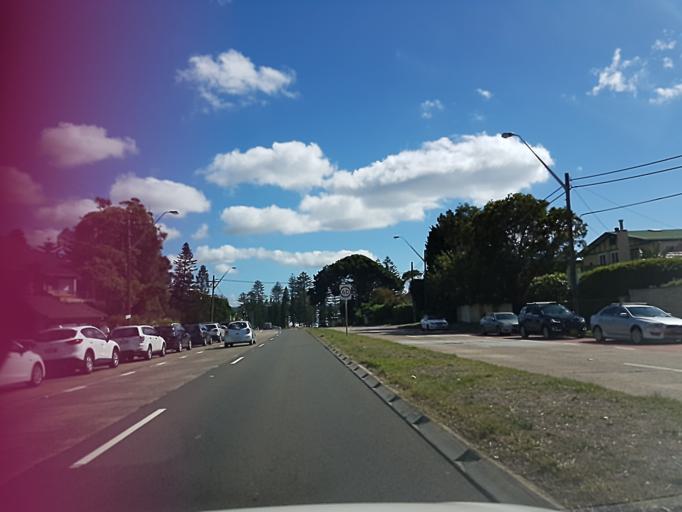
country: AU
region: New South Wales
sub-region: Warringah
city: Dee Why
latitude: -33.7358
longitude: 151.3023
